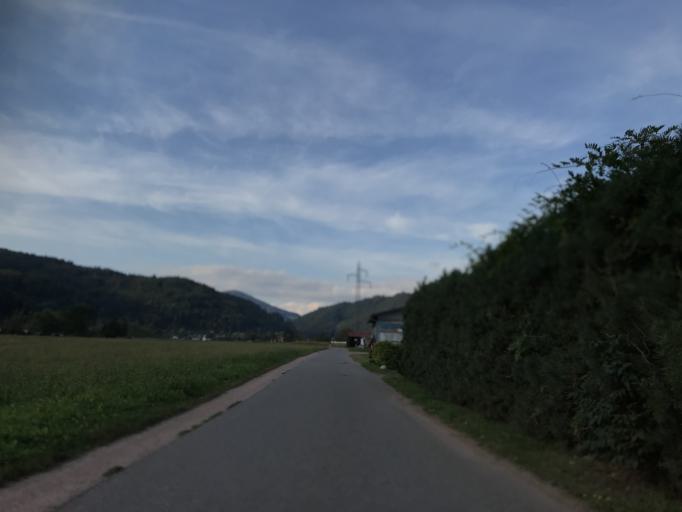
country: DE
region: Baden-Wuerttemberg
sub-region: Freiburg Region
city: Hausen
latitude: 47.6694
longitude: 7.8329
